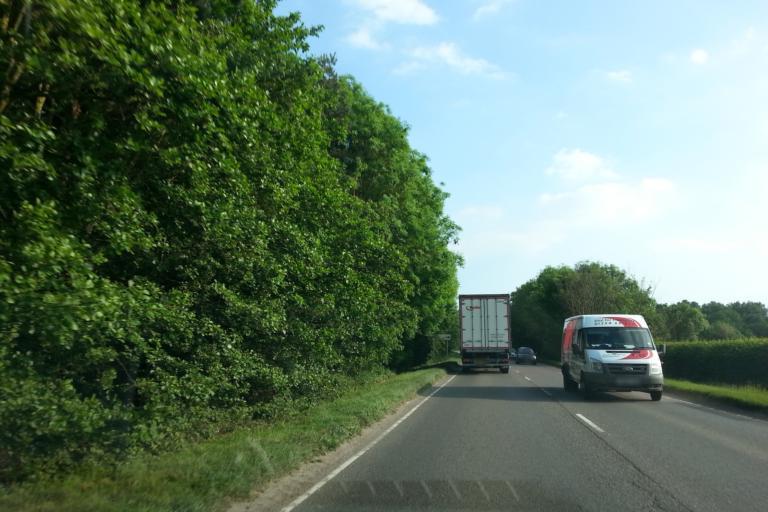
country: GB
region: England
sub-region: Cambridgeshire
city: Hemingford Grey
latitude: 52.3105
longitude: -0.0858
